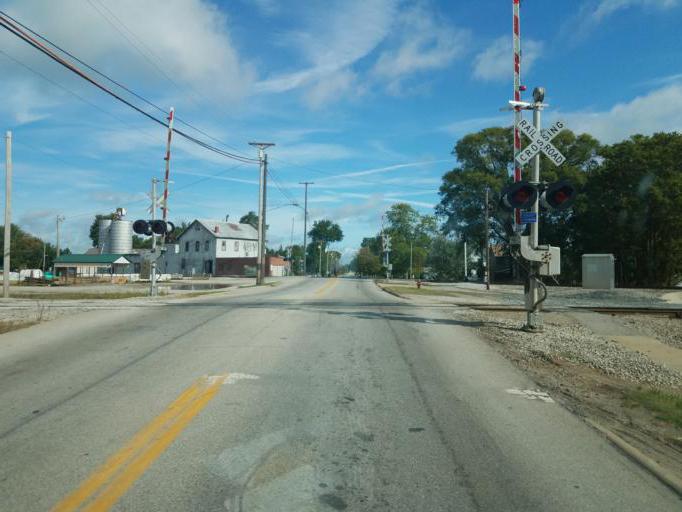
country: US
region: Ohio
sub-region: Lorain County
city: Wellington
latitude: 41.1030
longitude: -82.1232
